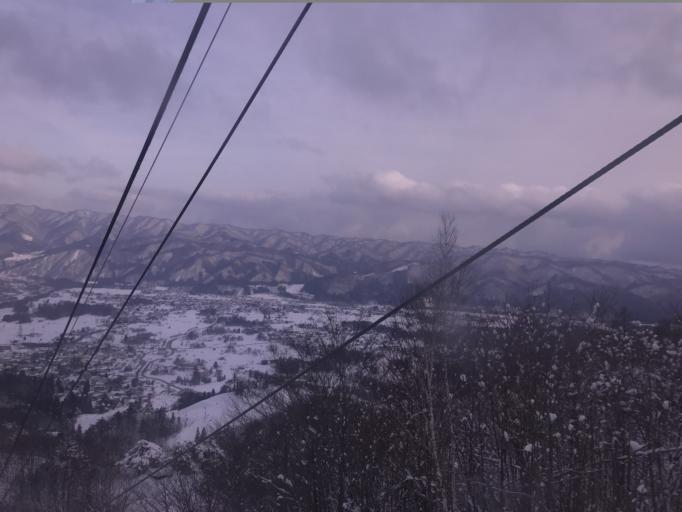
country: JP
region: Nagano
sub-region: Kitaazumi Gun
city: Hakuba
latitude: 36.6998
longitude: 137.8272
